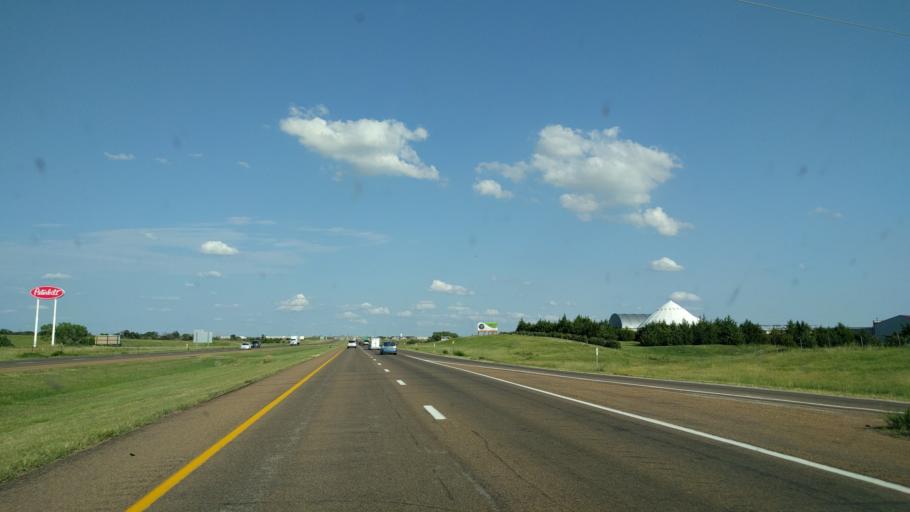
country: US
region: Kansas
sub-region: Ellis County
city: Hays
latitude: 38.9115
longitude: -99.3524
